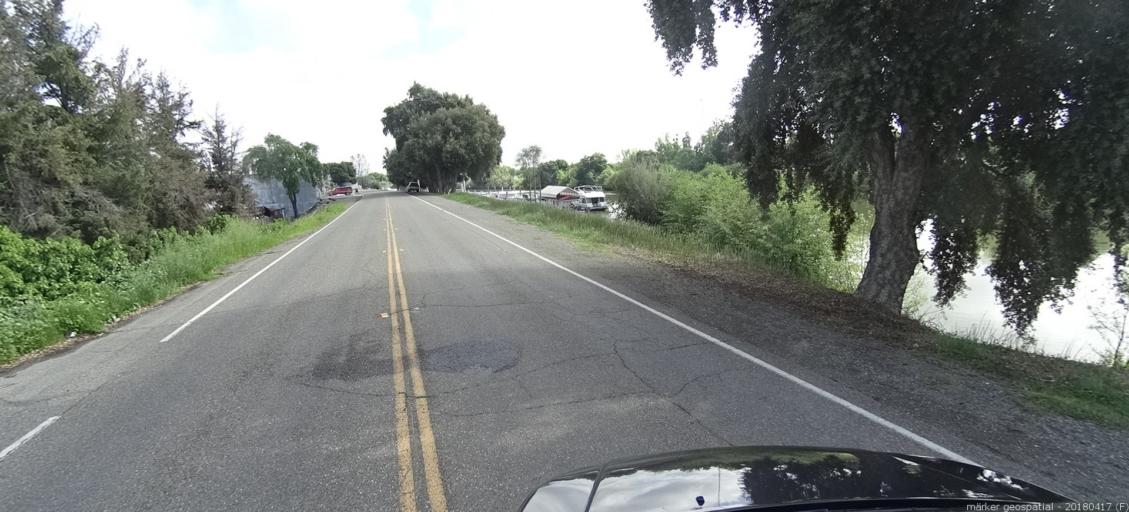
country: US
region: California
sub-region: Sacramento County
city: Walnut Grove
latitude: 38.2438
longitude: -121.5144
